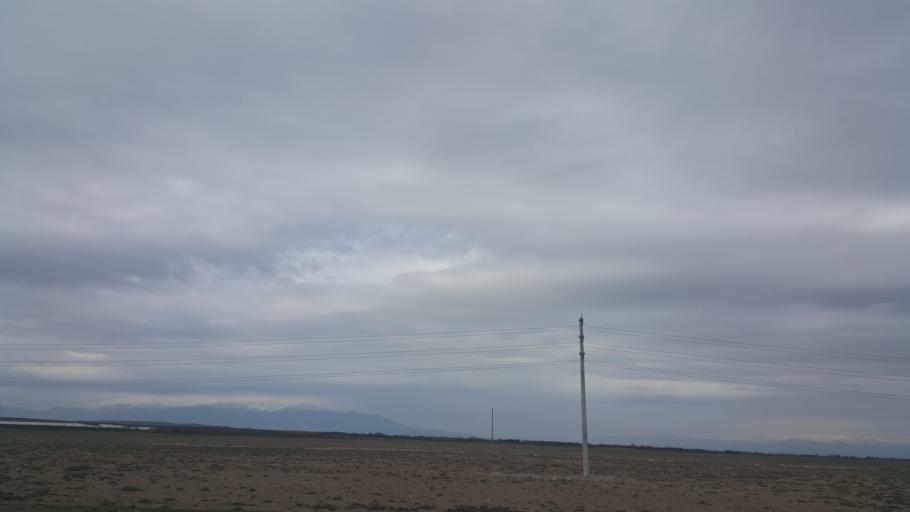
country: TR
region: Nigde
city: Altunhisar
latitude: 37.7847
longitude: 34.2331
